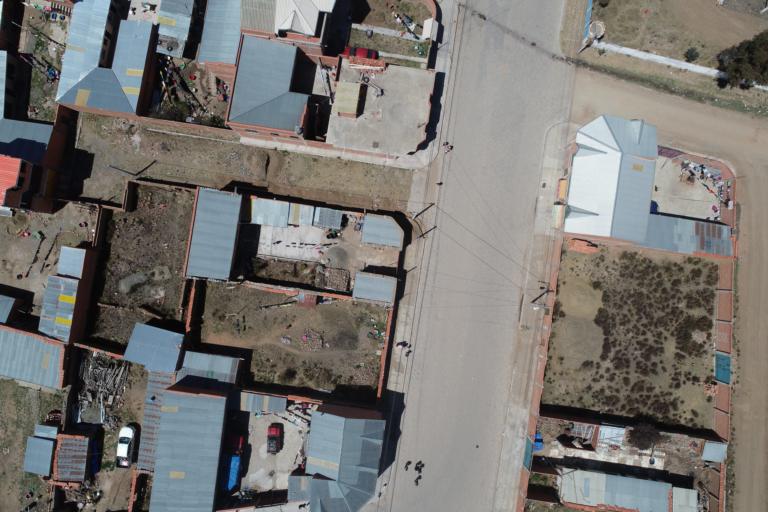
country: BO
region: La Paz
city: La Paz
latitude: -16.5660
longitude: -68.1916
